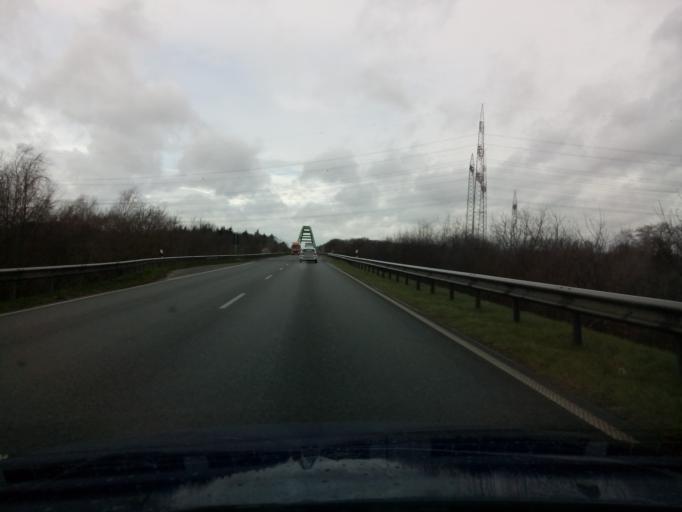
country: DE
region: Lower Saxony
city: Meppen
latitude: 52.7213
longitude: 7.2721
